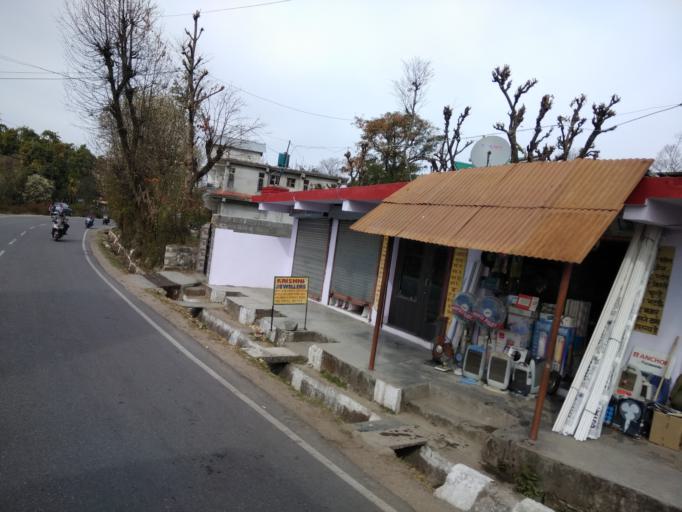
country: IN
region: Himachal Pradesh
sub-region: Kangra
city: Dharmsala
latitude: 32.1866
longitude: 76.3628
